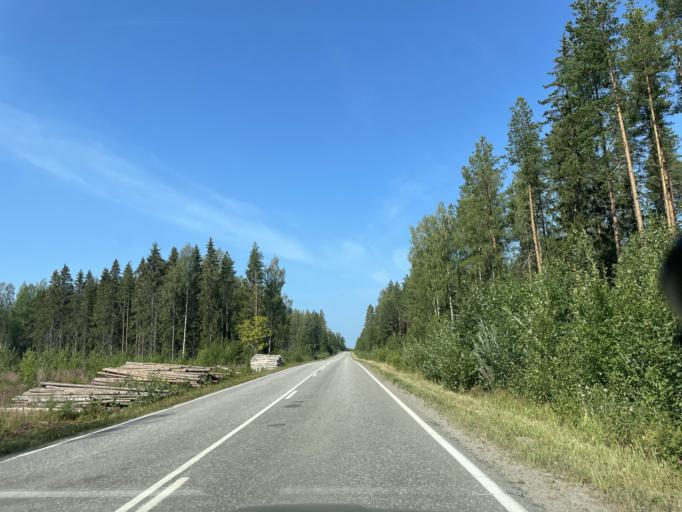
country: FI
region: Central Finland
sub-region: Saarijaervi-Viitasaari
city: Pihtipudas
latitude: 63.3678
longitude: 25.6267
